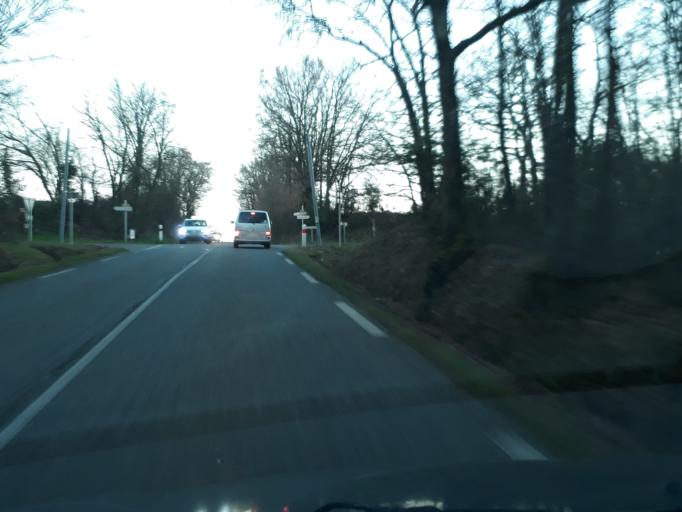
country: FR
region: Midi-Pyrenees
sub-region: Departement du Gers
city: Pujaudran
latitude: 43.5633
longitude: 1.1278
